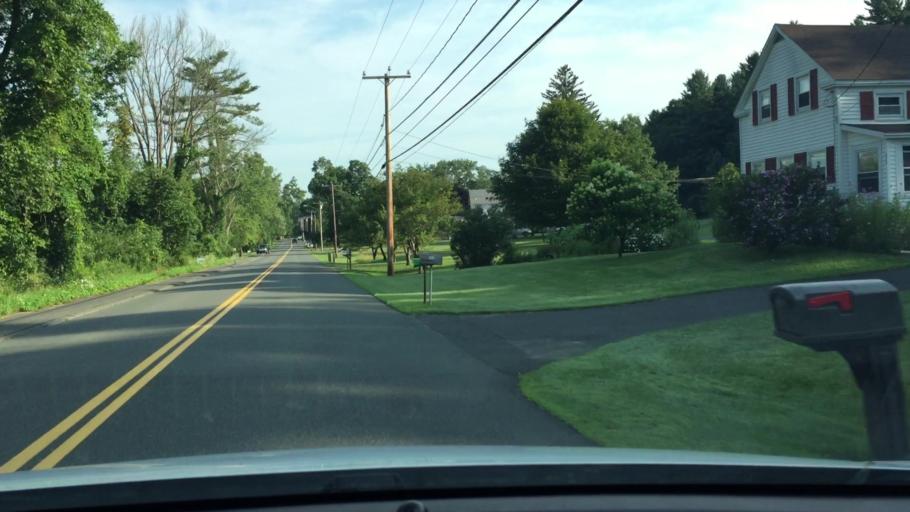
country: US
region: Massachusetts
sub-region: Berkshire County
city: Lee
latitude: 42.3193
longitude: -73.2364
